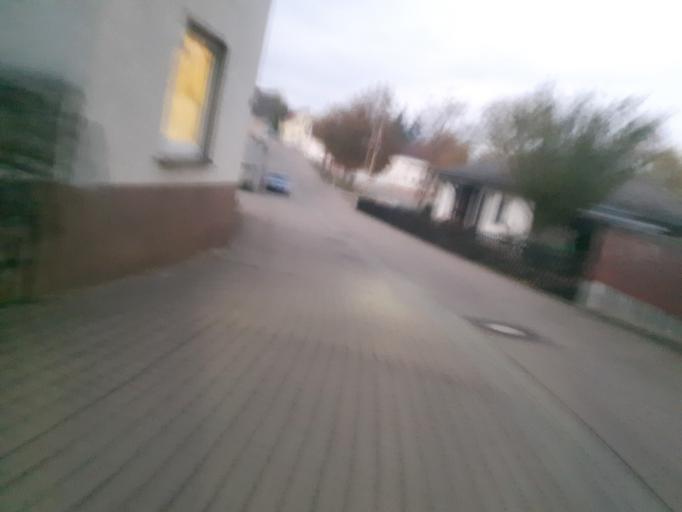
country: DE
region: Rheinland-Pfalz
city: Ober-Florsheim
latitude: 49.6853
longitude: 8.1572
